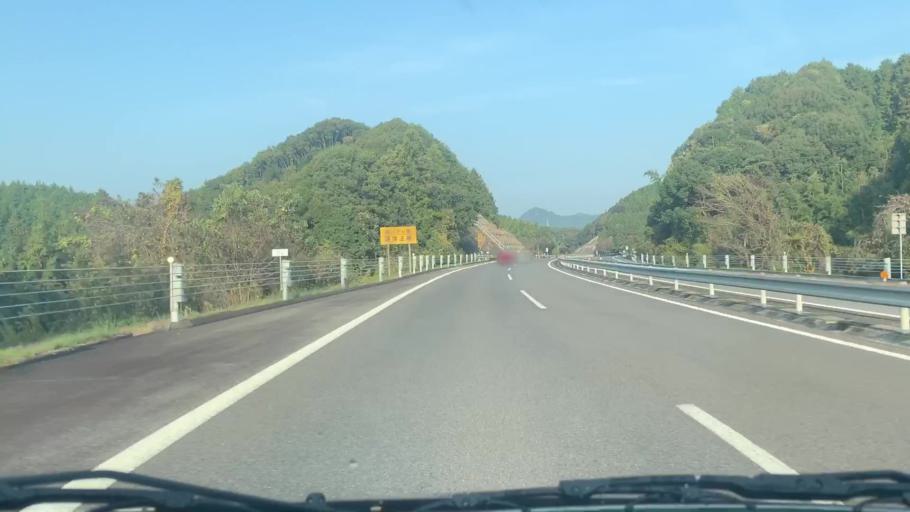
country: JP
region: Saga Prefecture
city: Ureshinomachi-shimojuku
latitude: 33.1502
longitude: 129.9364
